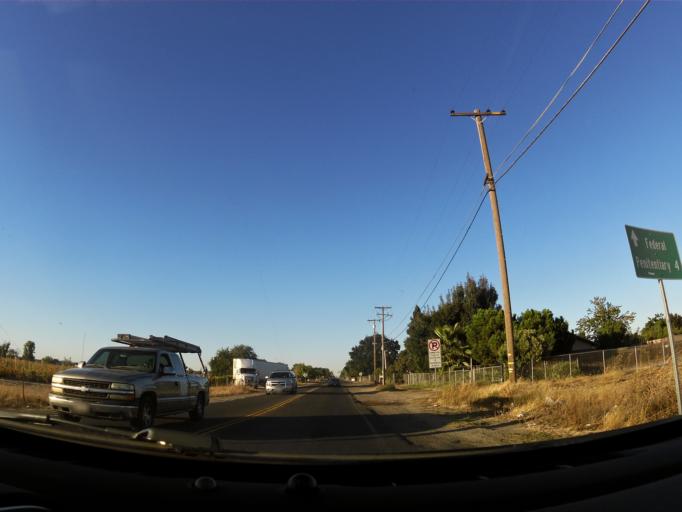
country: US
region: California
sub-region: Merced County
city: Merced
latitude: 37.3232
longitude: -120.5410
